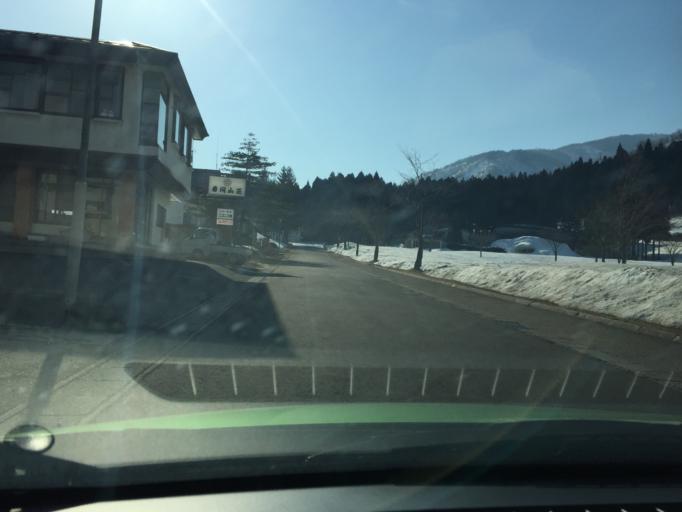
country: JP
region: Ishikawa
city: Tsurugi-asahimachi
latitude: 36.2679
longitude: 136.7164
